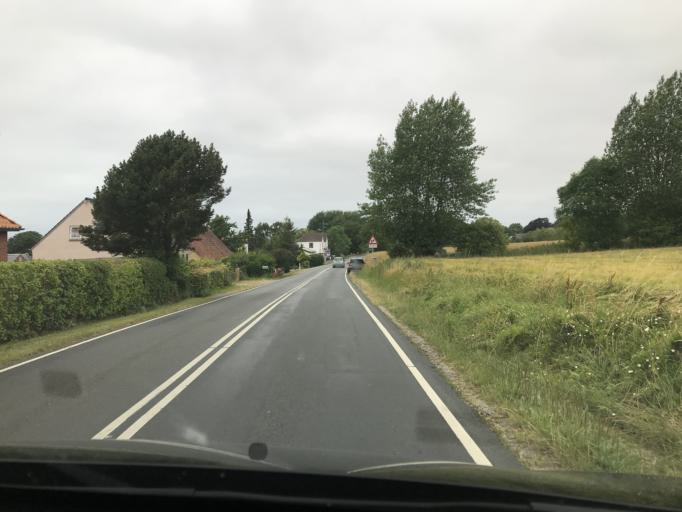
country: DK
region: South Denmark
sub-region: AEro Kommune
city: AEroskobing
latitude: 54.8692
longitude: 10.3605
